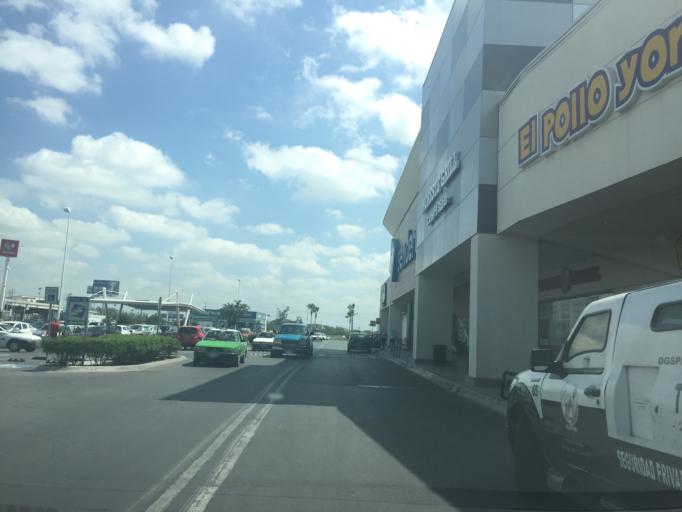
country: MX
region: Nuevo Leon
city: Apodaca
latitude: 25.7644
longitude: -100.1912
